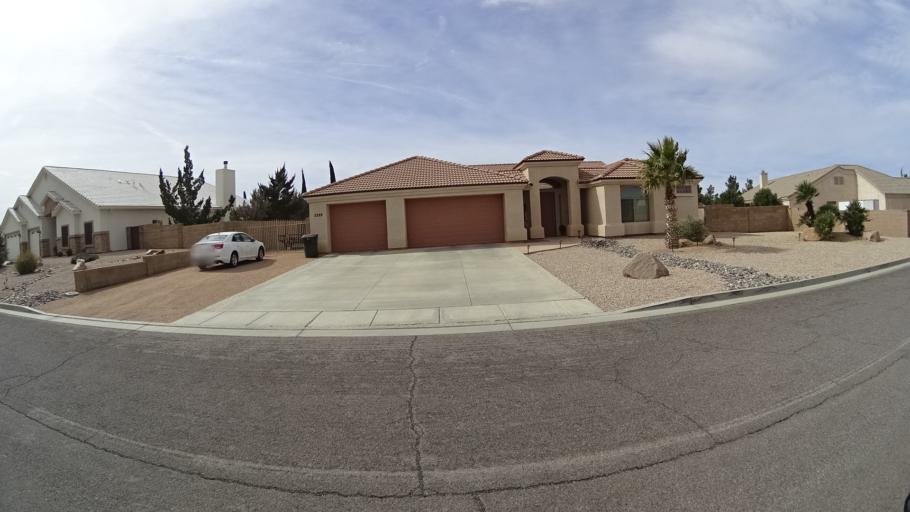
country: US
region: Arizona
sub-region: Mohave County
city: Kingman
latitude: 35.1898
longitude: -113.9794
